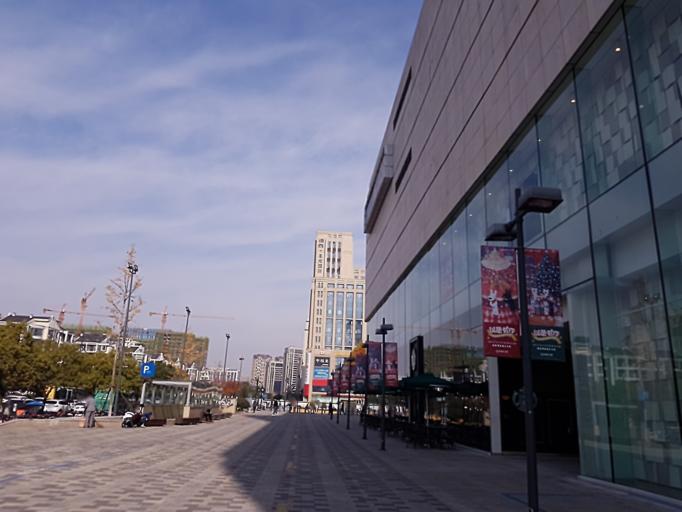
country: CN
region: Zhejiang Sheng
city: Xiangfu
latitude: 30.3015
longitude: 120.1012
